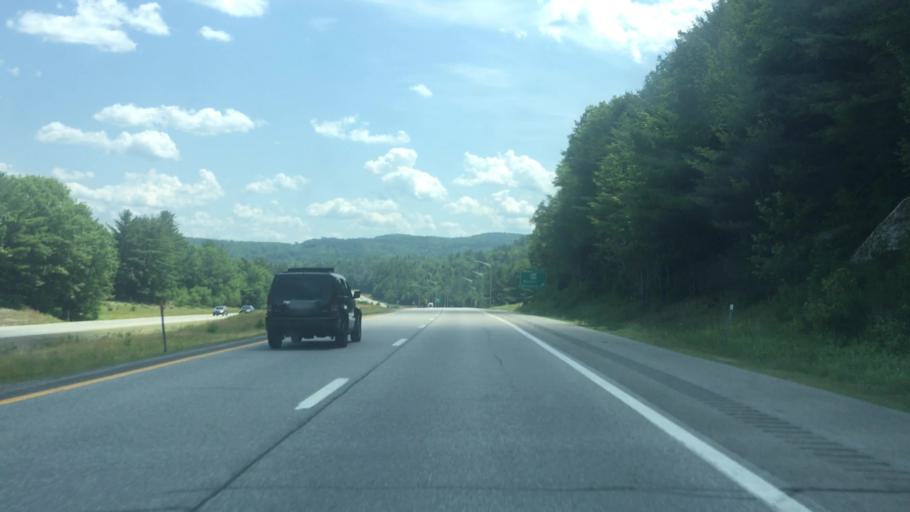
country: US
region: New Hampshire
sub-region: Merrimack County
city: Henniker
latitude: 43.2944
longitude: -71.8389
